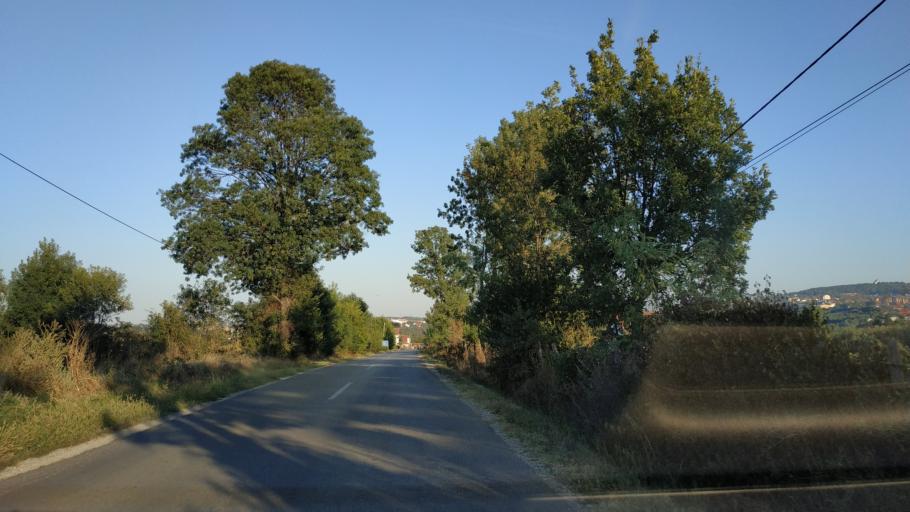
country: RS
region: Central Serbia
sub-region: Sumadijski Okrug
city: Topola
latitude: 44.2672
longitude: 20.6648
